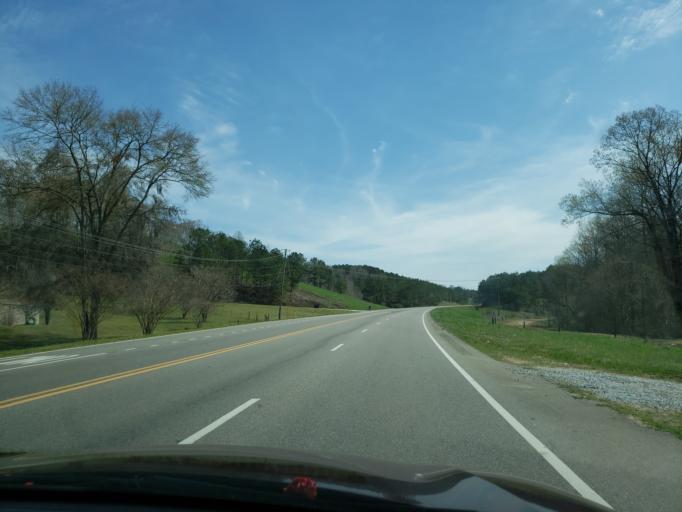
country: US
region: Alabama
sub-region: Autauga County
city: Prattville
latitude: 32.4329
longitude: -86.5649
